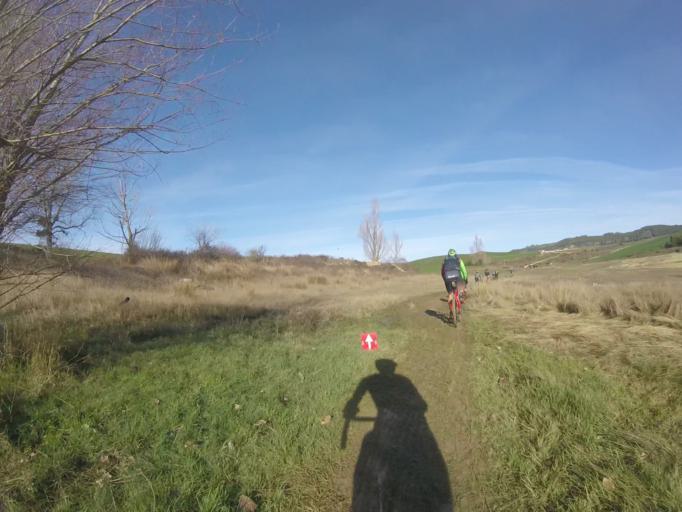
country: ES
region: Navarre
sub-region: Provincia de Navarra
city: Yerri
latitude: 42.7122
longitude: -1.9583
